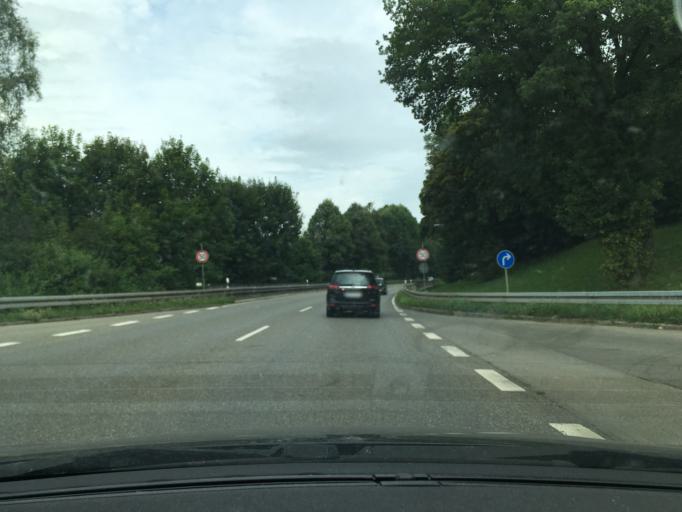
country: DE
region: Baden-Wuerttemberg
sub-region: Tuebingen Region
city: Uberlingen
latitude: 47.7594
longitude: 9.1949
